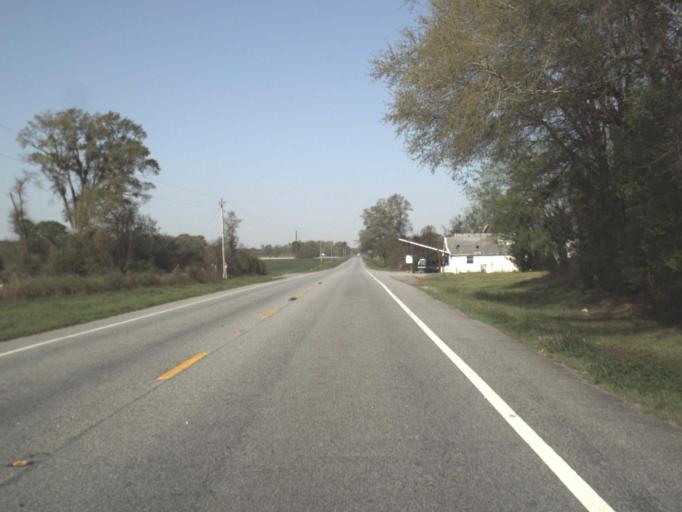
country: US
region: Florida
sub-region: Jackson County
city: Malone
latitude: 30.9760
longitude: -85.0407
